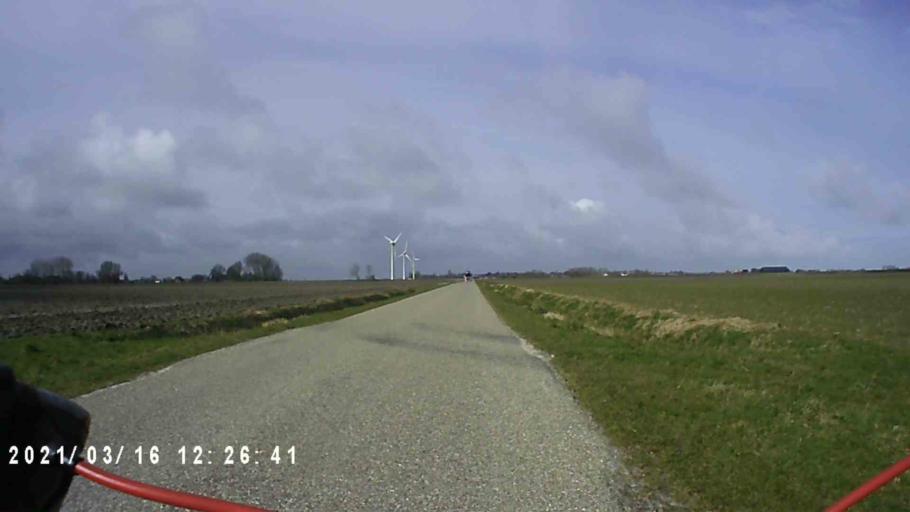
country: NL
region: Friesland
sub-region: Gemeente Leeuwarderadeel
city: Stiens
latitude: 53.2966
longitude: 5.7433
